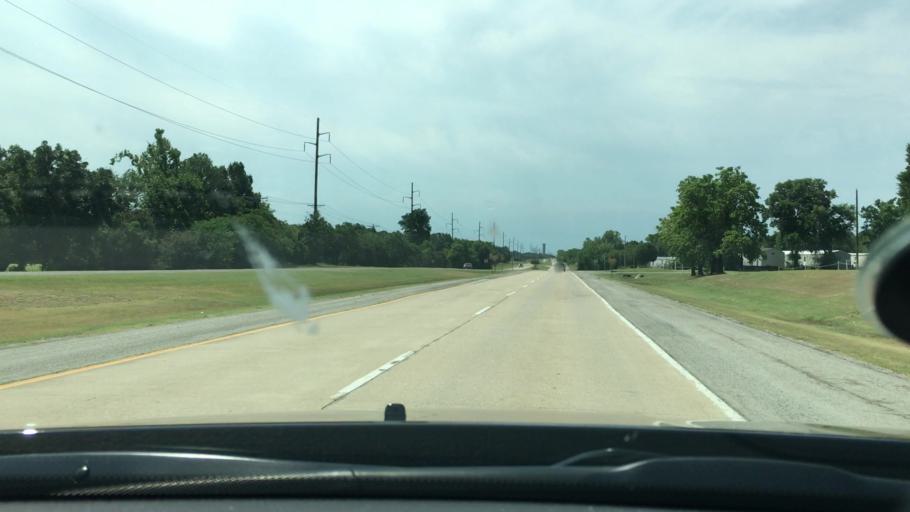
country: US
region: Oklahoma
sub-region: Carter County
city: Ardmore
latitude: 34.2217
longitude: -97.1433
